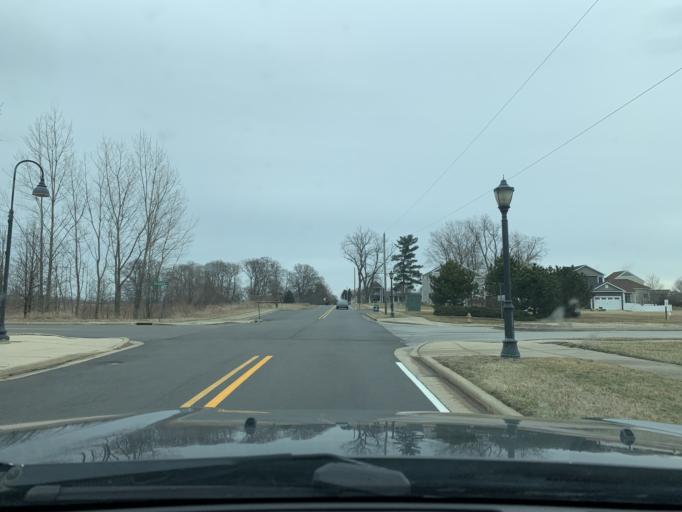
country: US
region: Indiana
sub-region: Porter County
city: Chesterton
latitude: 41.5863
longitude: -87.0356
